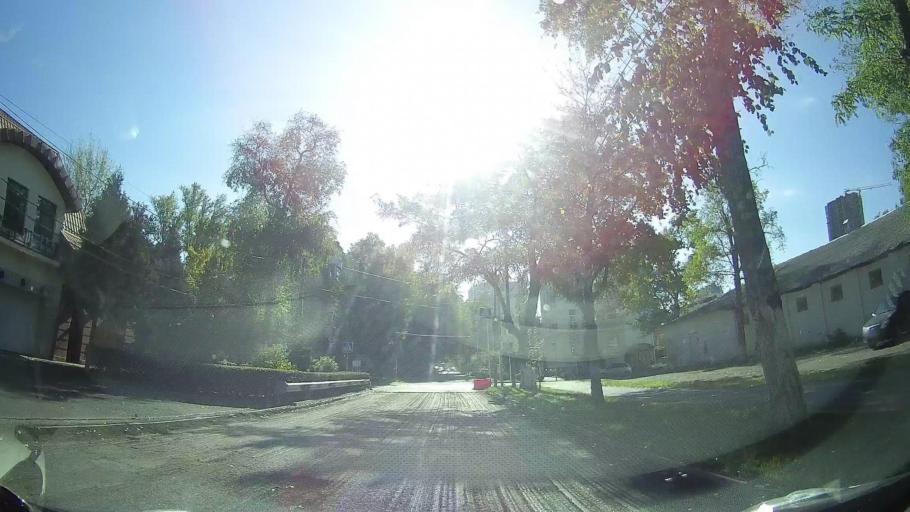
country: RU
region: Rostov
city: Rostov-na-Donu
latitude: 47.2364
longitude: 39.7298
